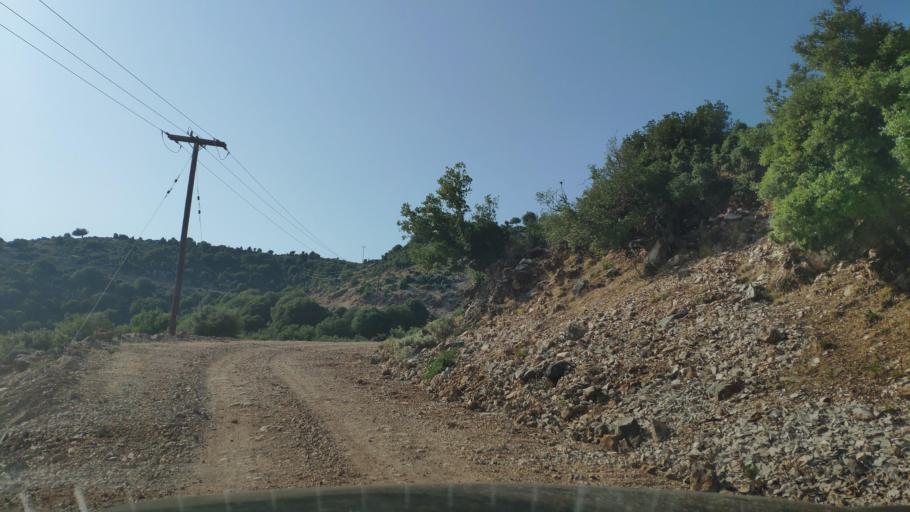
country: GR
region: West Greece
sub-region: Nomos Aitolias kai Akarnanias
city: Monastirakion
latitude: 38.8324
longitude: 20.9726
